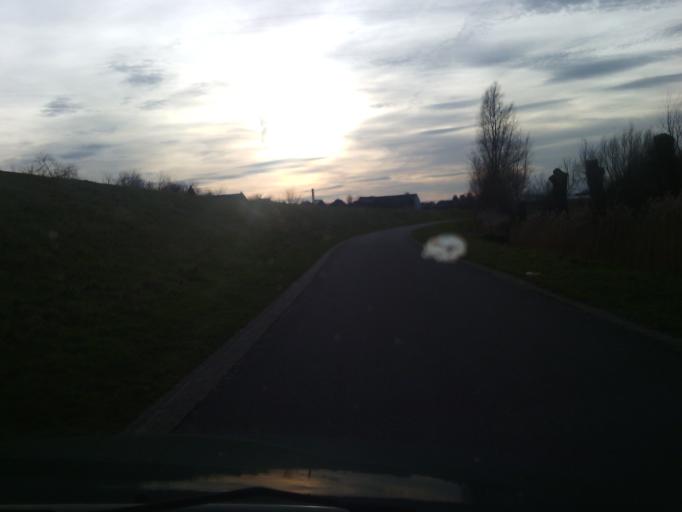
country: BE
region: Flanders
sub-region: Provincie Oost-Vlaanderen
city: Berlare
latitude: 51.0086
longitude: 4.0184
